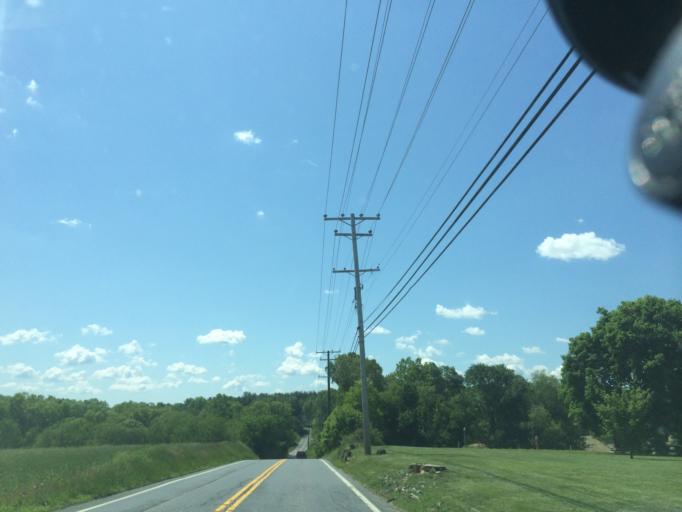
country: US
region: Maryland
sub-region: Carroll County
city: Sykesville
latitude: 39.3760
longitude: -77.0177
